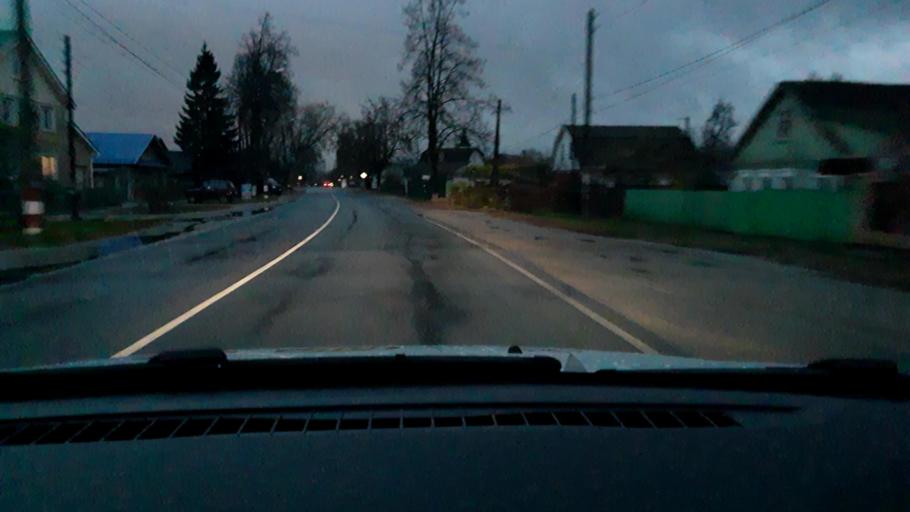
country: RU
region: Nizjnij Novgorod
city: Bor
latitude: 56.3687
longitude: 44.0372
